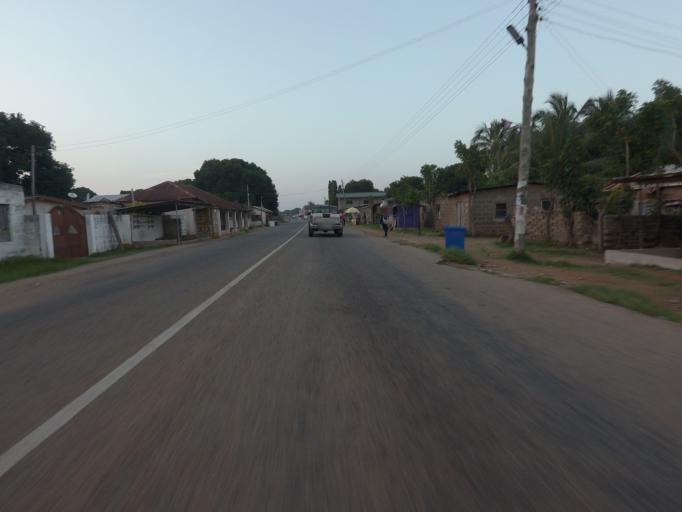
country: GH
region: Volta
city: Keta
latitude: 5.8596
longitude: 0.9777
